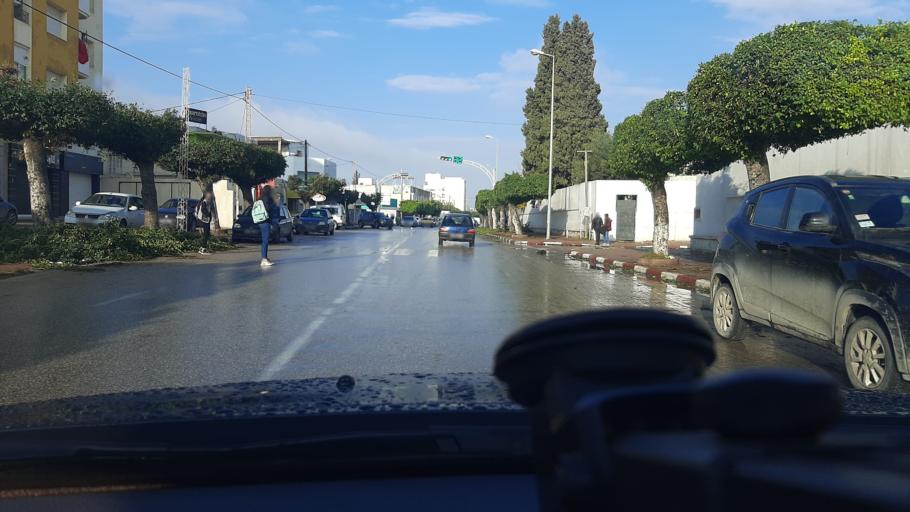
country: TN
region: Safaqis
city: Sfax
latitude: 34.7435
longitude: 10.7473
